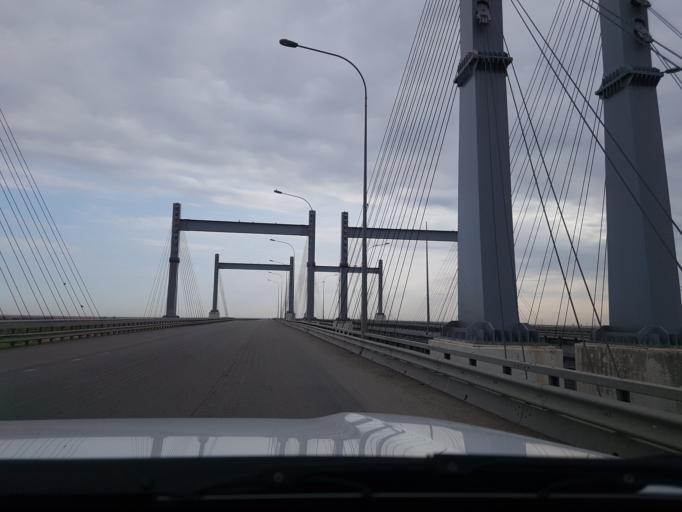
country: TM
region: Ahal
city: Tejen
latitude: 37.2317
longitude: 60.1503
